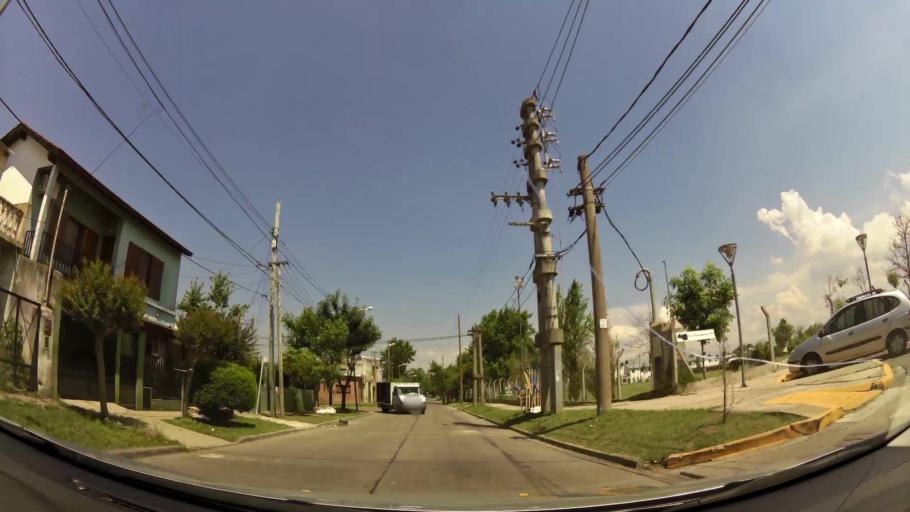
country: AR
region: Buenos Aires
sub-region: Partido de Tigre
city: Tigre
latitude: -34.4558
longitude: -58.5806
